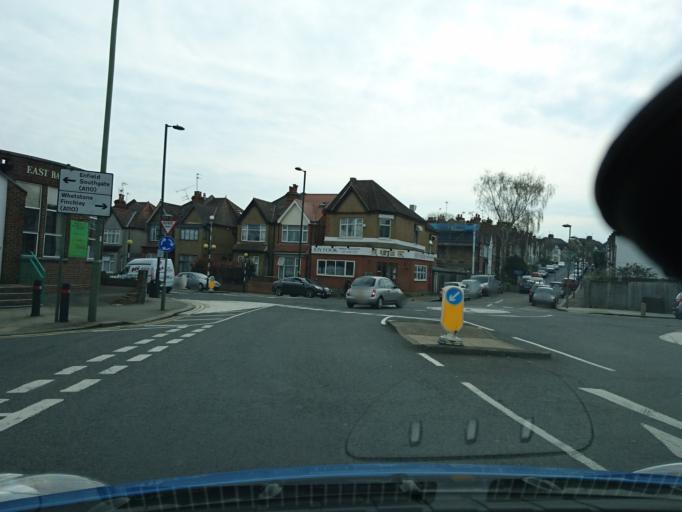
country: GB
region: England
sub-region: Greater London
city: Hadley Wood
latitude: 51.6436
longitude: -0.1655
